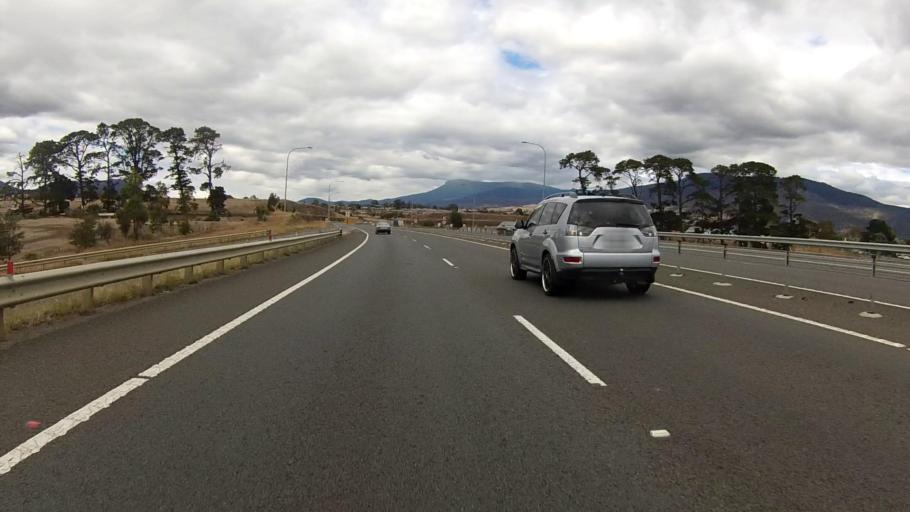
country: AU
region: Tasmania
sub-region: Brighton
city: Bridgewater
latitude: -42.7268
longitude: 147.2373
